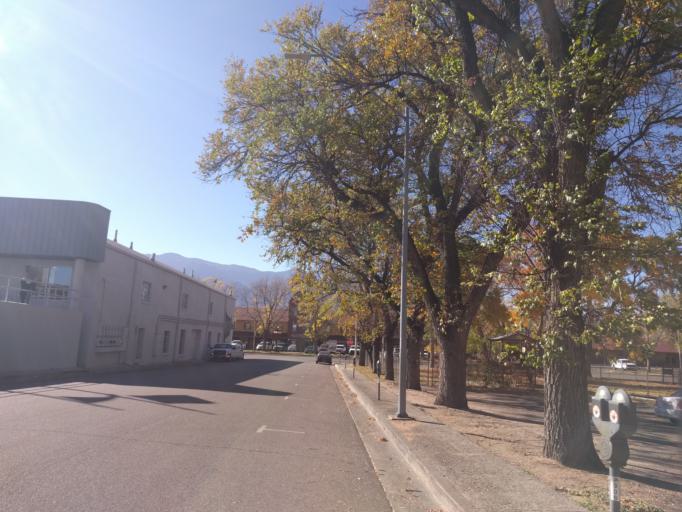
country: US
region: Colorado
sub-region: El Paso County
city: Colorado Springs
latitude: 38.8331
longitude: -104.8278
